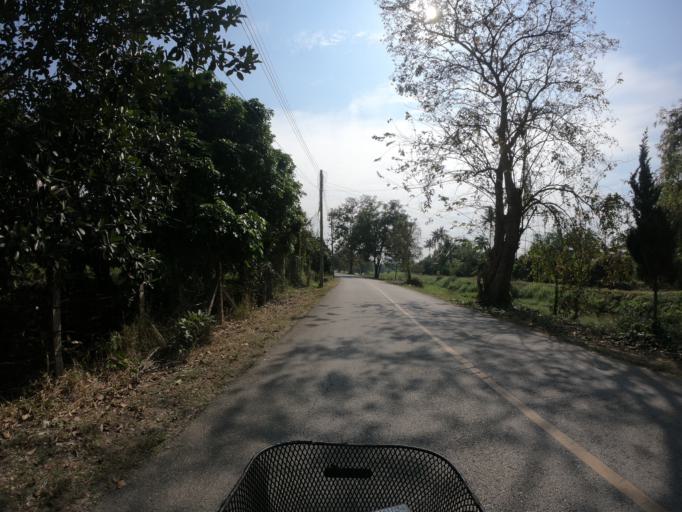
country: TH
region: Chiang Mai
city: Saraphi
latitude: 18.7010
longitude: 99.0565
